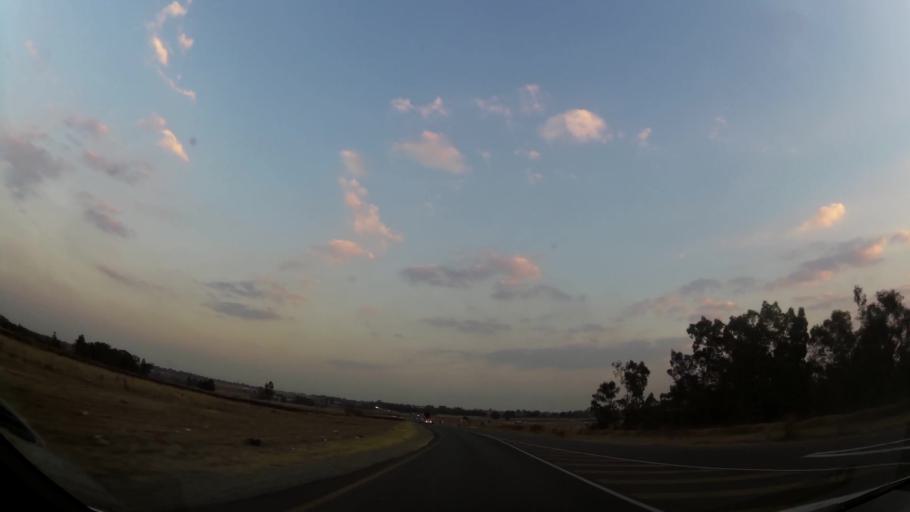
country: ZA
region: Gauteng
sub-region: Ekurhuleni Metropolitan Municipality
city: Springs
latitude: -26.2791
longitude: 28.4295
